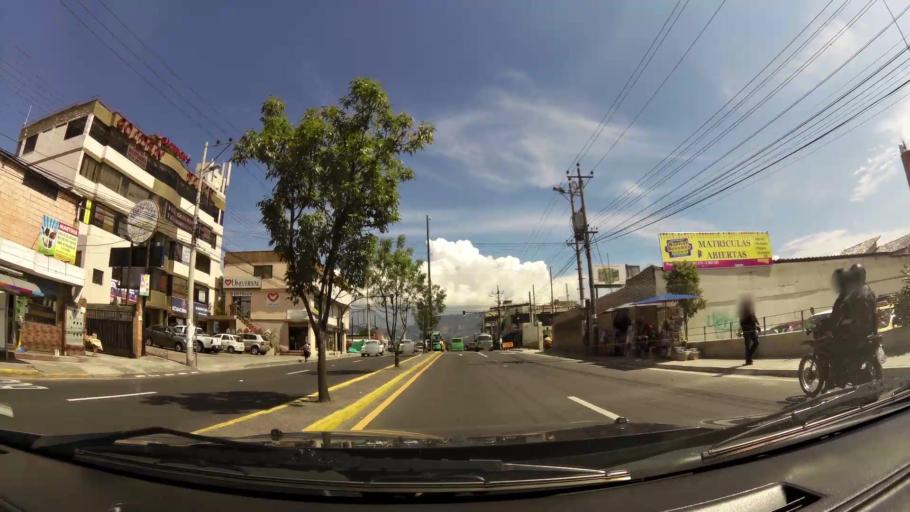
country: EC
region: Pichincha
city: Quito
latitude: -0.2157
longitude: -78.4043
